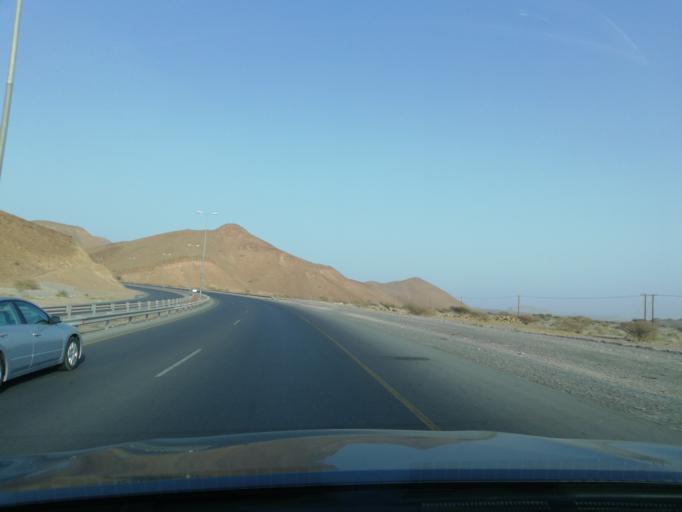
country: OM
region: Muhafazat ad Dakhiliyah
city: Izki
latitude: 22.8816
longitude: 57.7050
